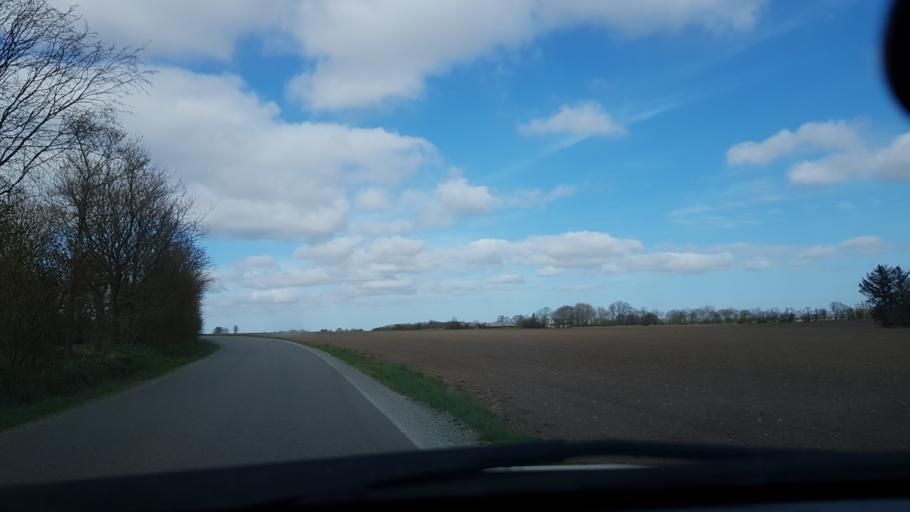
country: DK
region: South Denmark
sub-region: Vejen Kommune
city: Rodding
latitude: 55.3903
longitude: 9.0068
